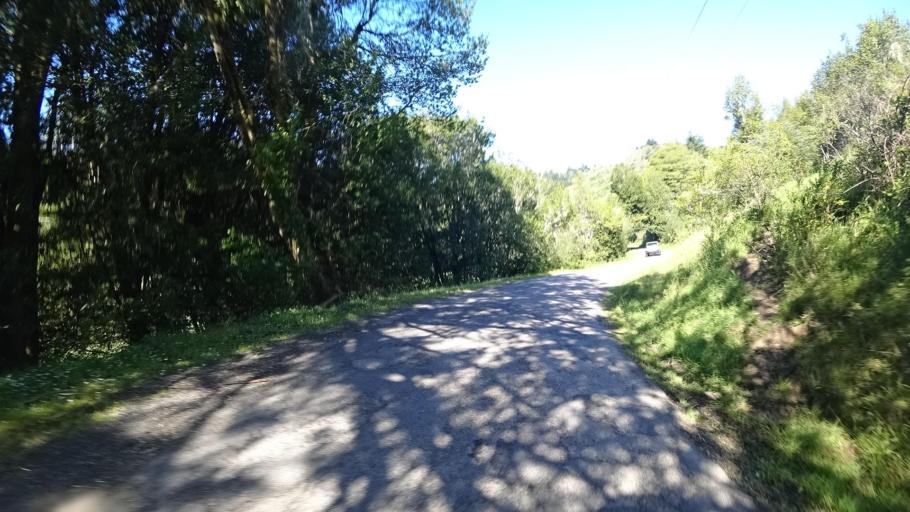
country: US
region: California
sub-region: Humboldt County
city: Fortuna
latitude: 40.5287
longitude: -124.1765
